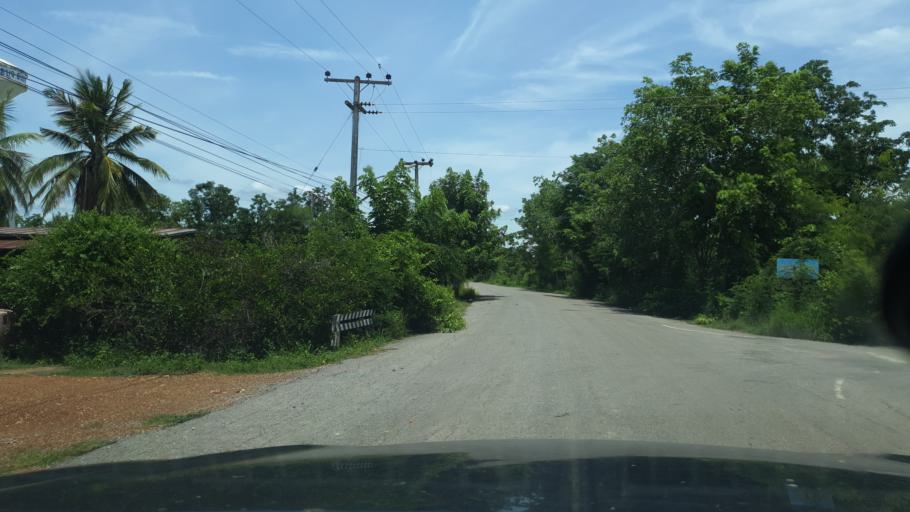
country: TH
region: Sukhothai
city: Ban Na
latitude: 17.0937
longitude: 99.6797
